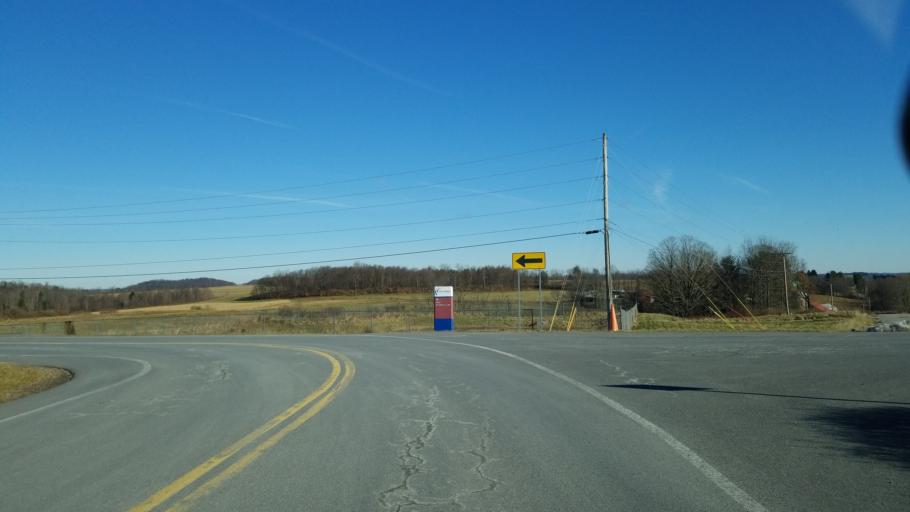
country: US
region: Pennsylvania
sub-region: Jefferson County
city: Reynoldsville
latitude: 41.1835
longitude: -78.8920
